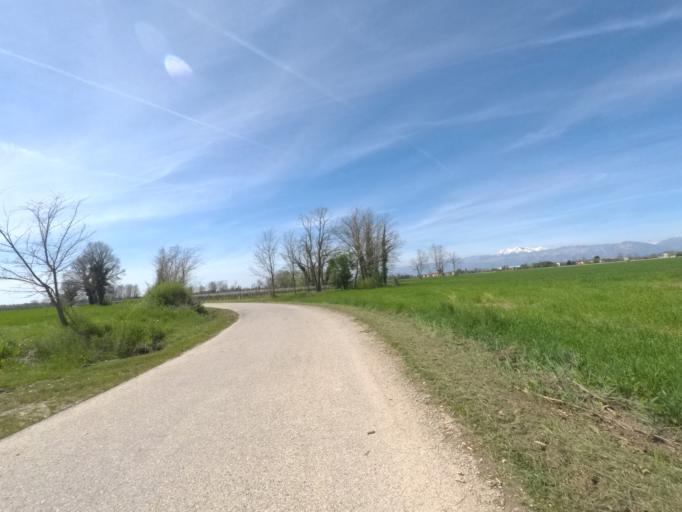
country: IT
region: Friuli Venezia Giulia
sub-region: Provincia di Pordenone
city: Rosa
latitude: 45.9533
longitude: 12.8669
